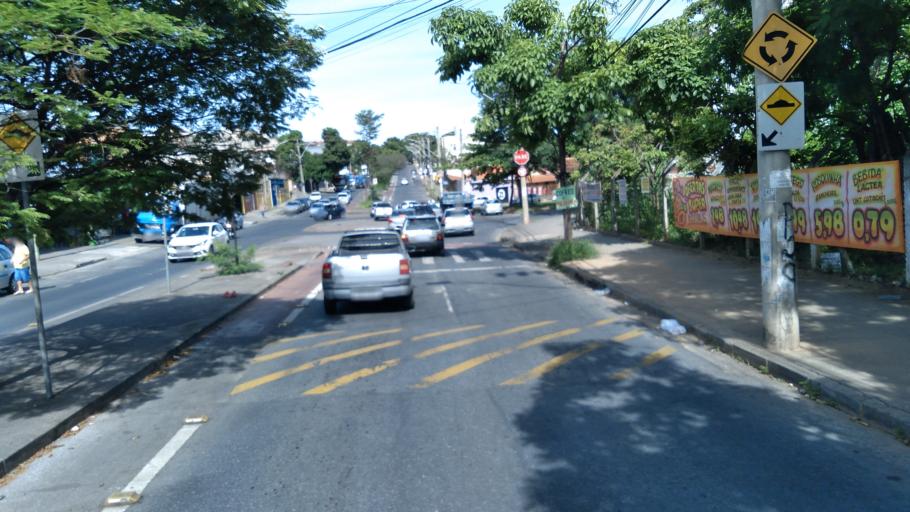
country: BR
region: Minas Gerais
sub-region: Contagem
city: Contagem
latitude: -19.8992
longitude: -44.0011
